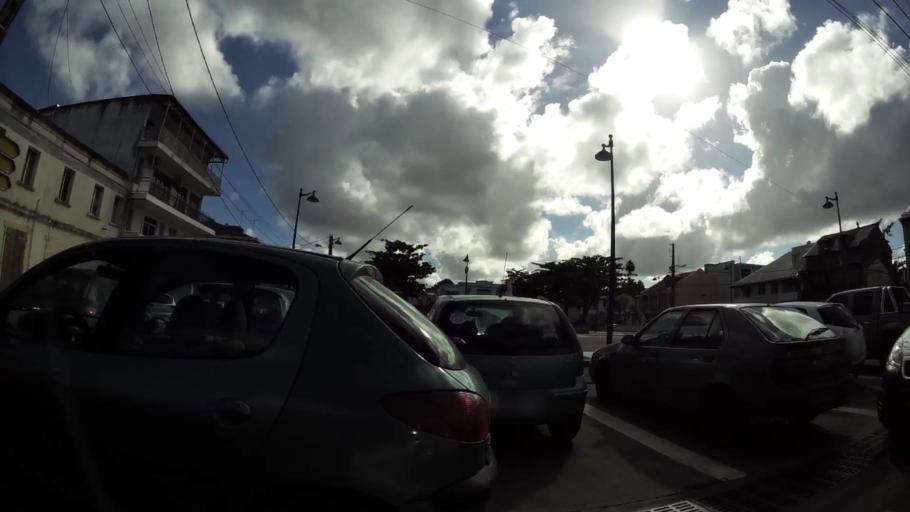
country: GP
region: Guadeloupe
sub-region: Guadeloupe
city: Petit-Canal
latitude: 16.3319
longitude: -61.4581
